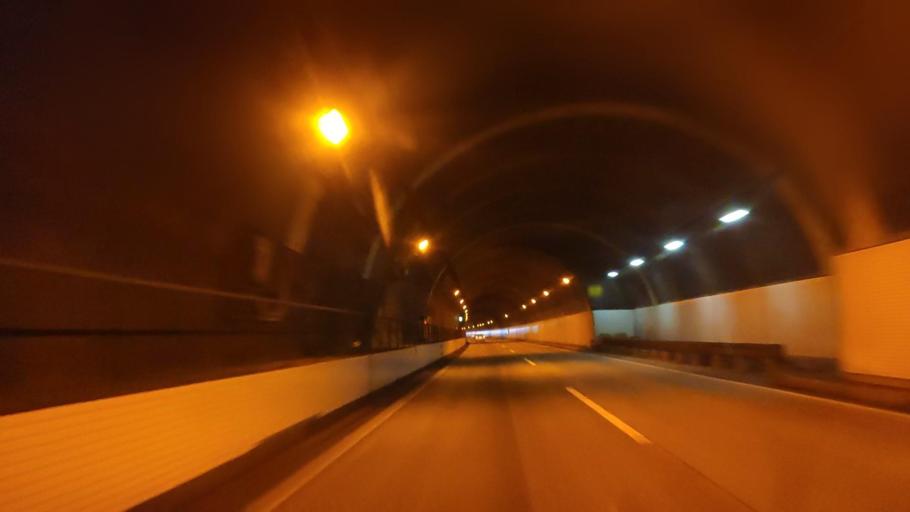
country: JP
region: Toyama
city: Nyuzen
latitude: 36.9720
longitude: 137.6344
